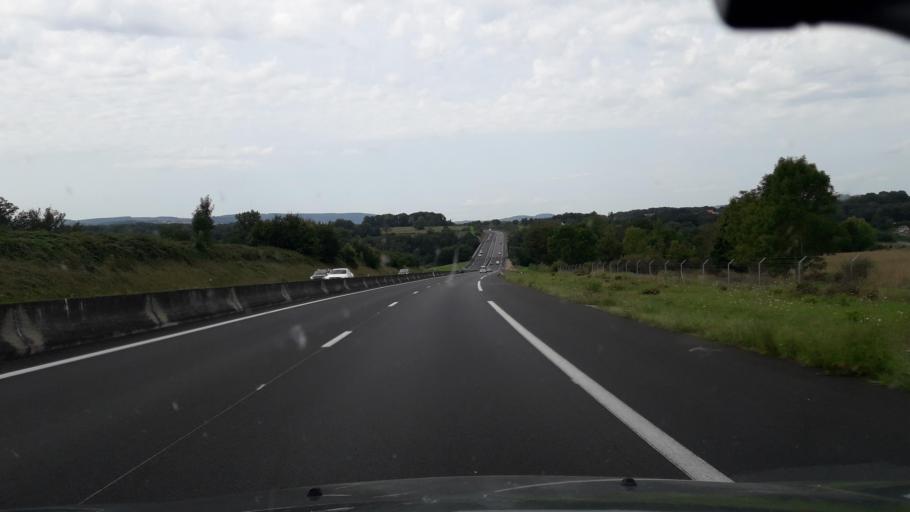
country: FR
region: Limousin
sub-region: Departement de la Creuse
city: Ajain
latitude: 46.1896
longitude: 1.9542
